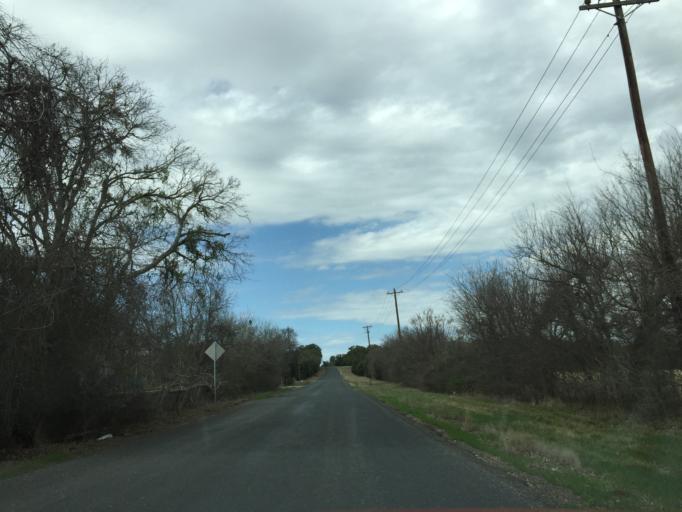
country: US
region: Texas
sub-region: Burnet County
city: Bertram
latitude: 30.7387
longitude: -97.9370
